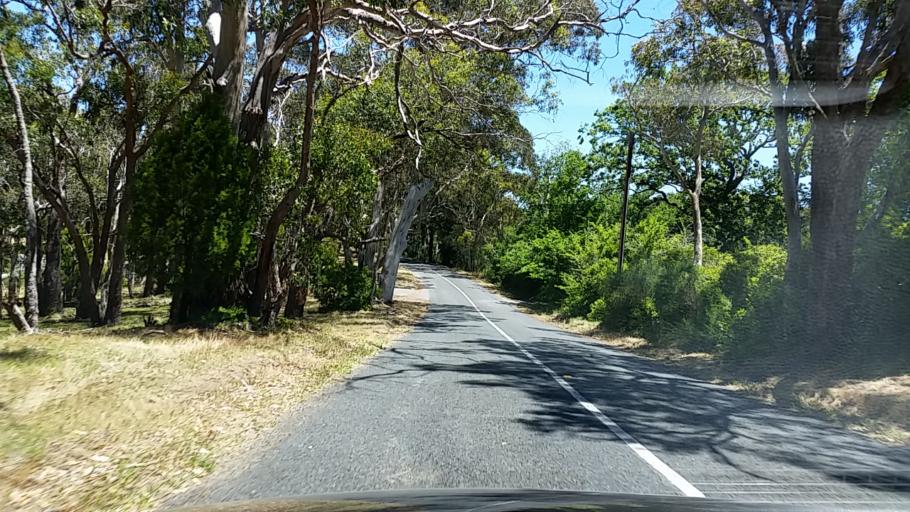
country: AU
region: South Australia
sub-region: Adelaide Hills
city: Crafers
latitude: -34.9981
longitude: 138.6906
